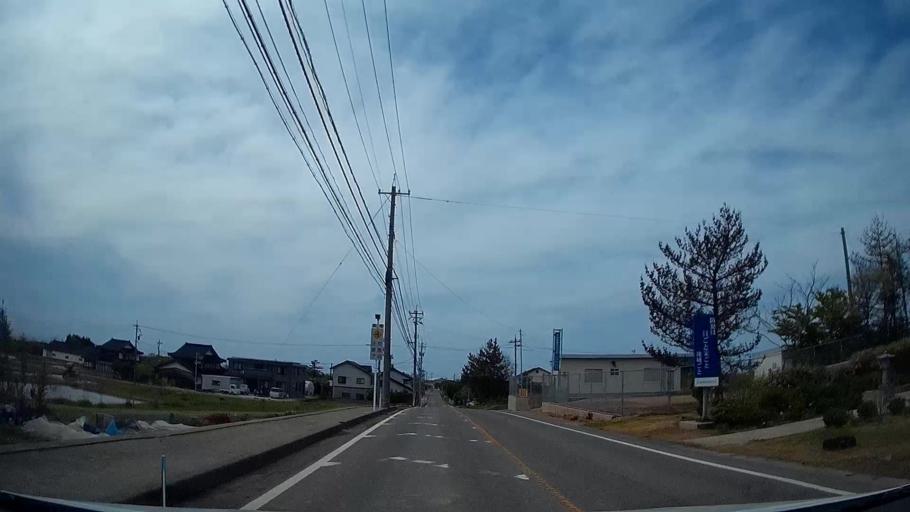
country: JP
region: Ishikawa
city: Hakui
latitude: 37.0165
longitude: 136.7514
